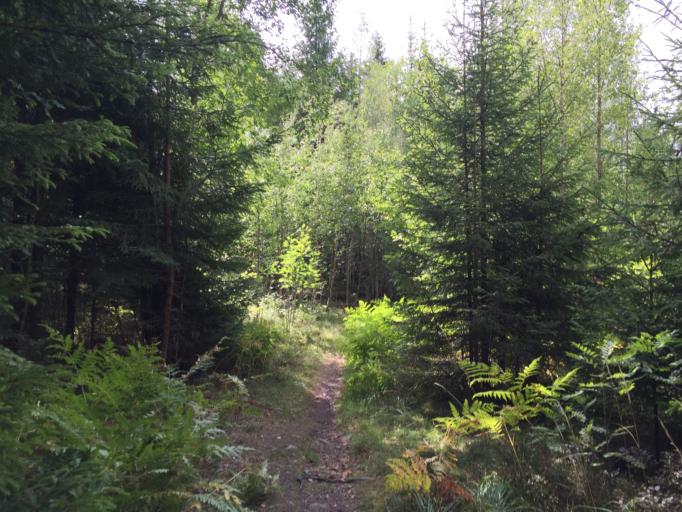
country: NO
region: Akershus
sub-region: Skedsmo
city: Lillestrom
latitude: 59.9223
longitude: 11.0117
